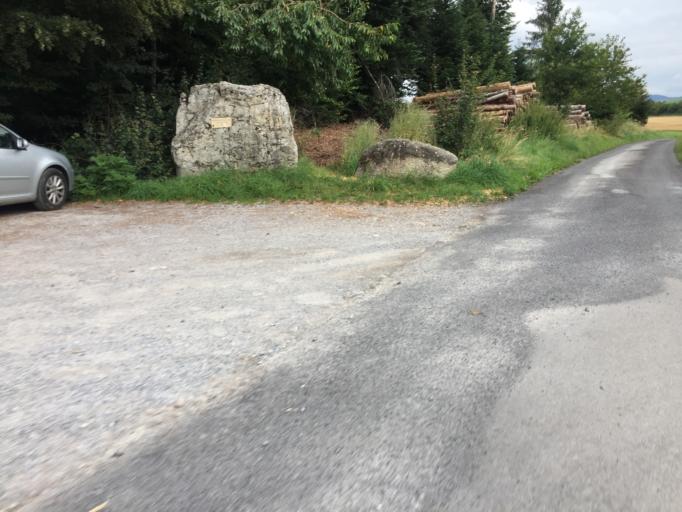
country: CH
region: Bern
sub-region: Bern-Mittelland District
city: Stettlen
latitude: 46.9422
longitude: 7.5266
